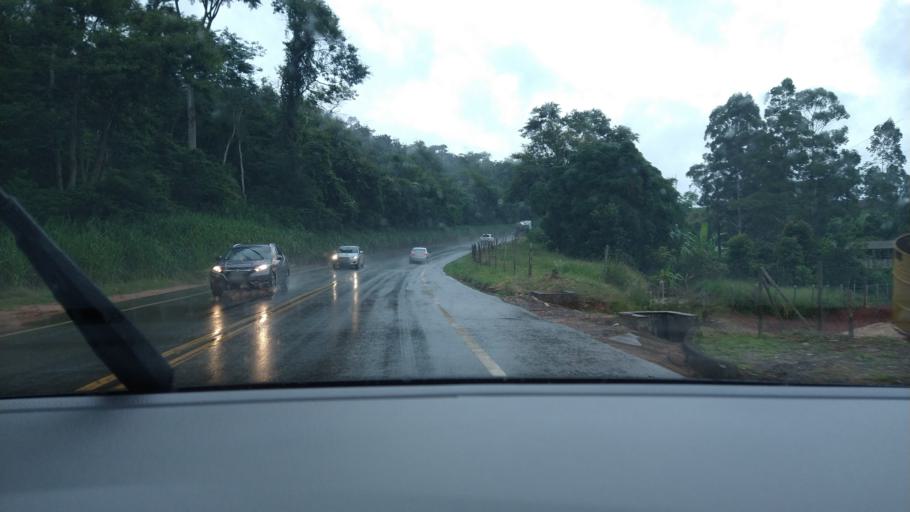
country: BR
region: Minas Gerais
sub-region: Vicosa
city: Vicosa
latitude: -20.6145
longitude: -42.8682
